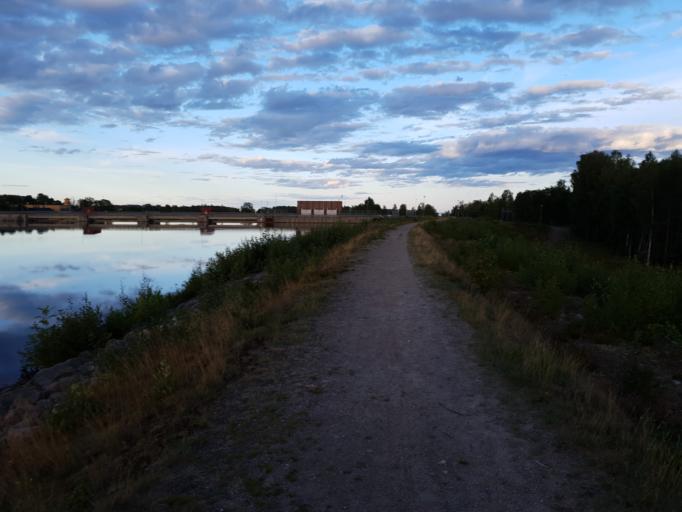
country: SE
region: Gaevleborg
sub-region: Soderhamns Kommun
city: Ljusne
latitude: 61.2063
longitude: 17.1168
